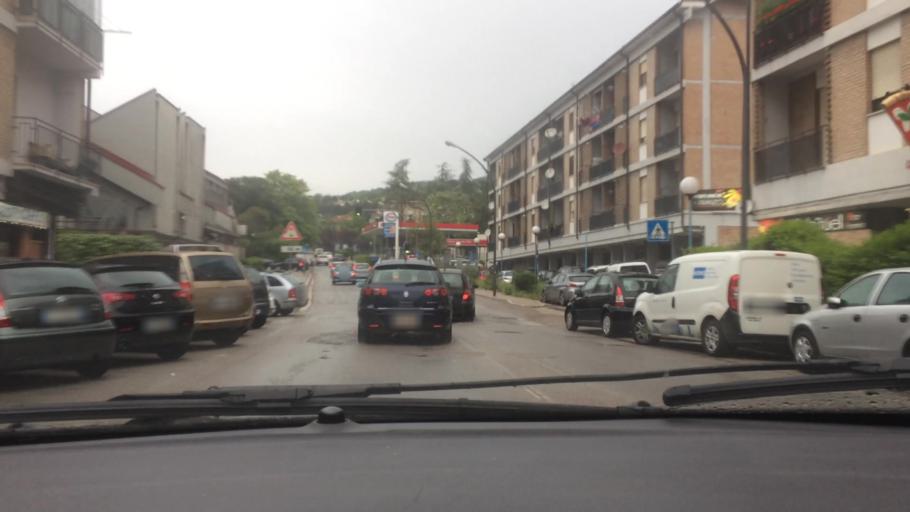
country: IT
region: Basilicate
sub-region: Provincia di Potenza
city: Potenza
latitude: 40.6476
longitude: 15.7972
